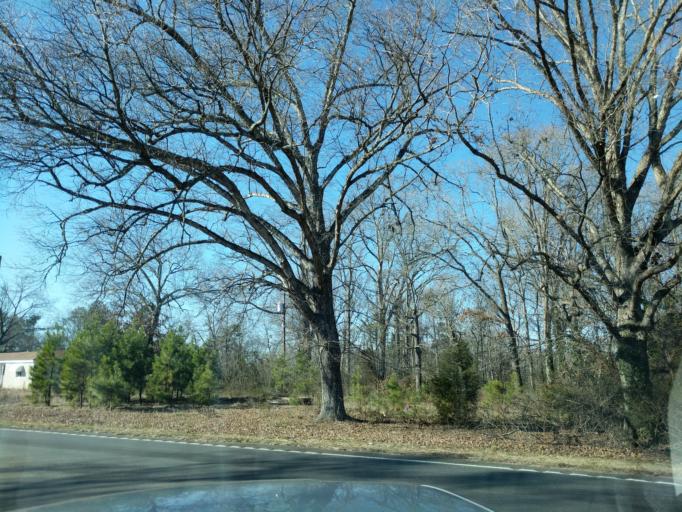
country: US
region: South Carolina
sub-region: Anderson County
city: Homeland Park
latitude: 34.4463
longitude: -82.7054
